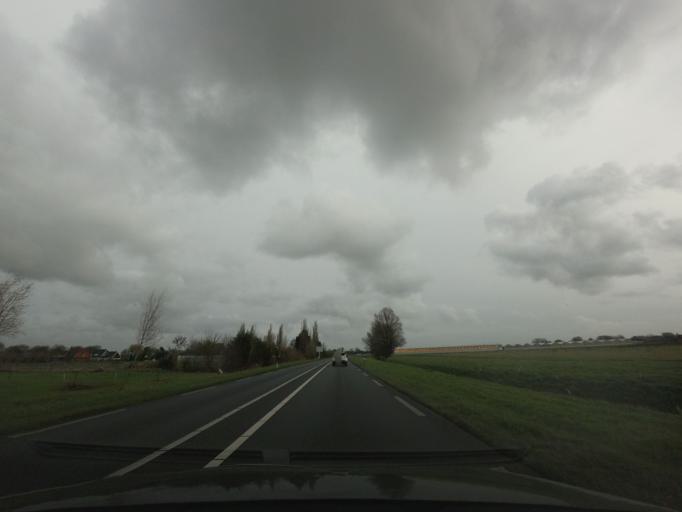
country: NL
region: North Holland
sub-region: Gemeente Langedijk
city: Broek op Langedijk
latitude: 52.7111
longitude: 4.8292
